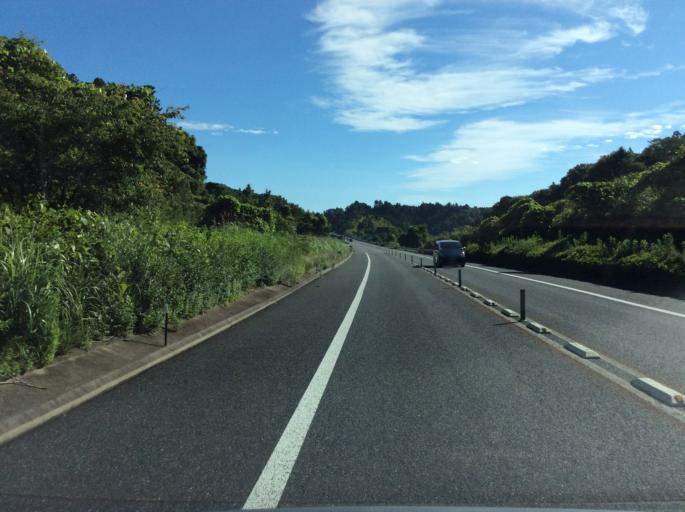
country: JP
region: Fukushima
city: Iwaki
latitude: 37.1770
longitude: 140.9764
